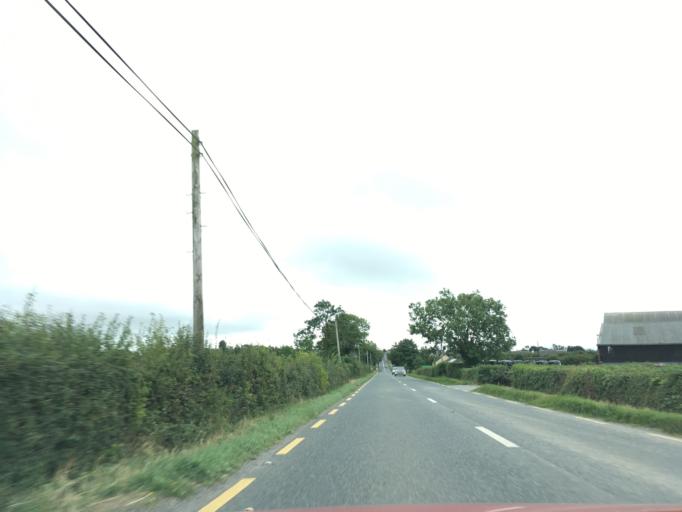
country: IE
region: Munster
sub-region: South Tipperary
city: Cluain Meala
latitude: 52.4172
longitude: -7.7611
